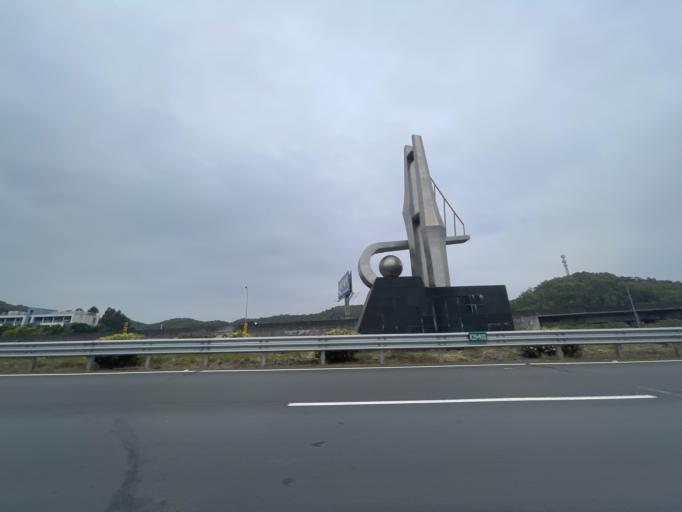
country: CN
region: Guangdong
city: Xinwan
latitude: 22.8070
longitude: 113.6345
